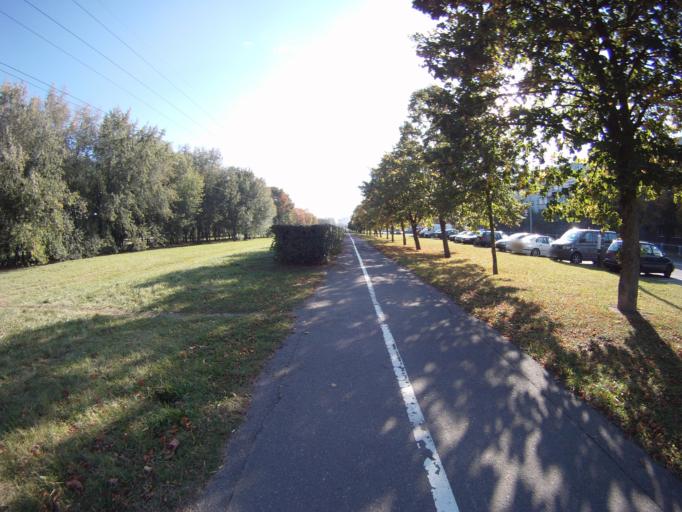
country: BY
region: Minsk
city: Minsk
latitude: 53.9381
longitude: 27.5663
